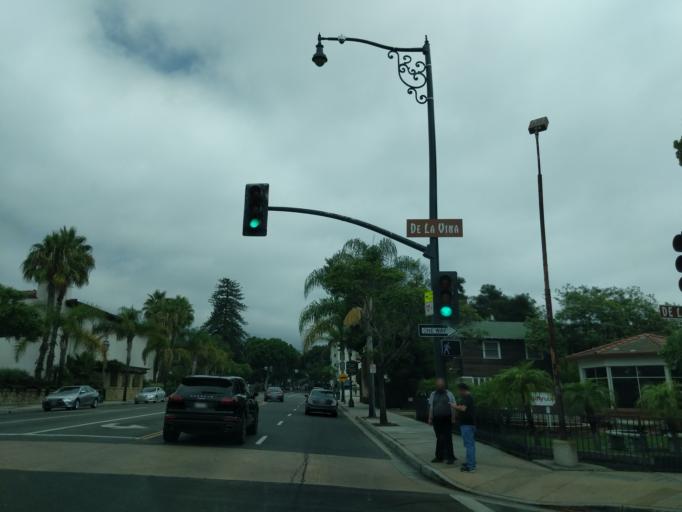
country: US
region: California
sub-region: Santa Barbara County
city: Santa Barbara
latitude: 34.4193
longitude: -119.7042
